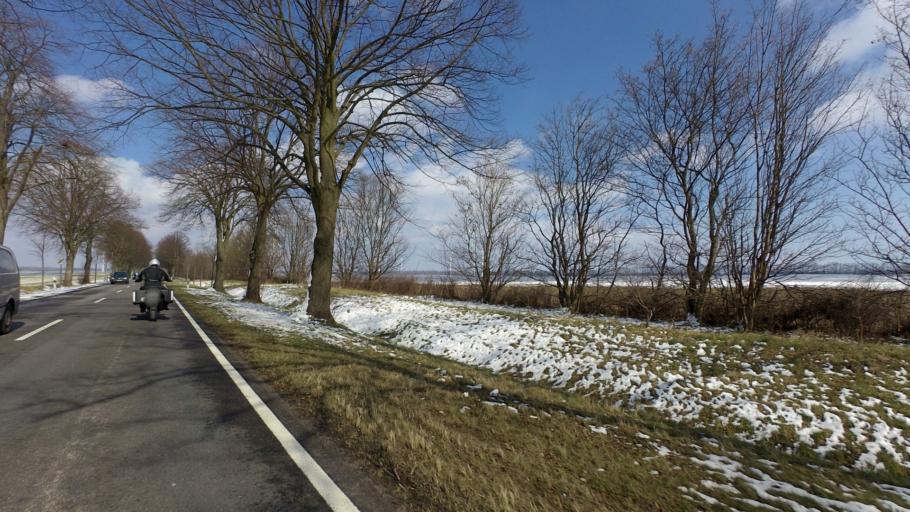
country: DE
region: Brandenburg
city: Eberswalde
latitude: 52.7475
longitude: 13.8444
